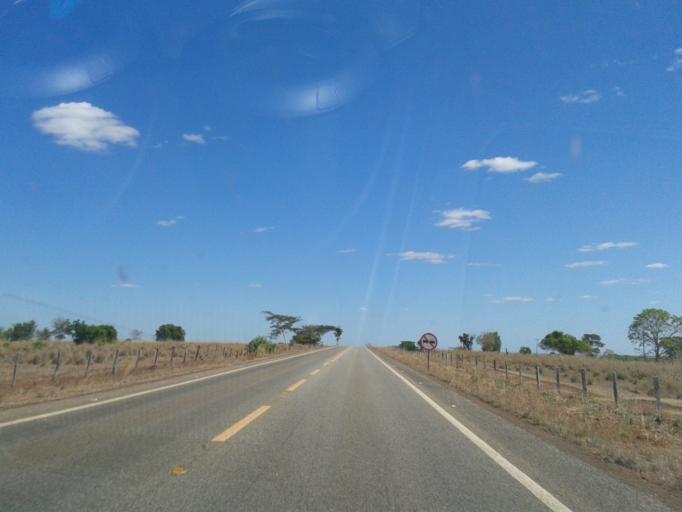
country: BR
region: Goias
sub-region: Sao Miguel Do Araguaia
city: Sao Miguel do Araguaia
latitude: -13.4134
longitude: -50.2679
